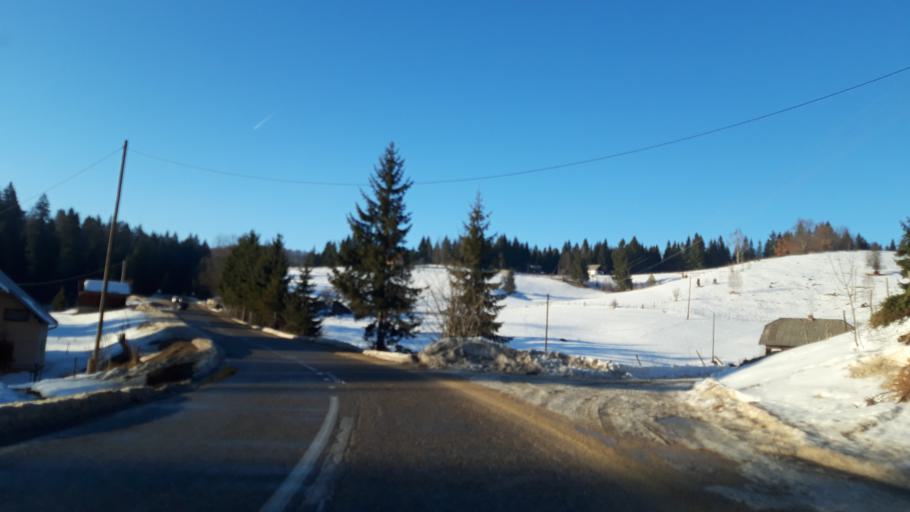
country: BA
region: Republika Srpska
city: Han Pijesak
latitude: 44.1212
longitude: 18.9687
